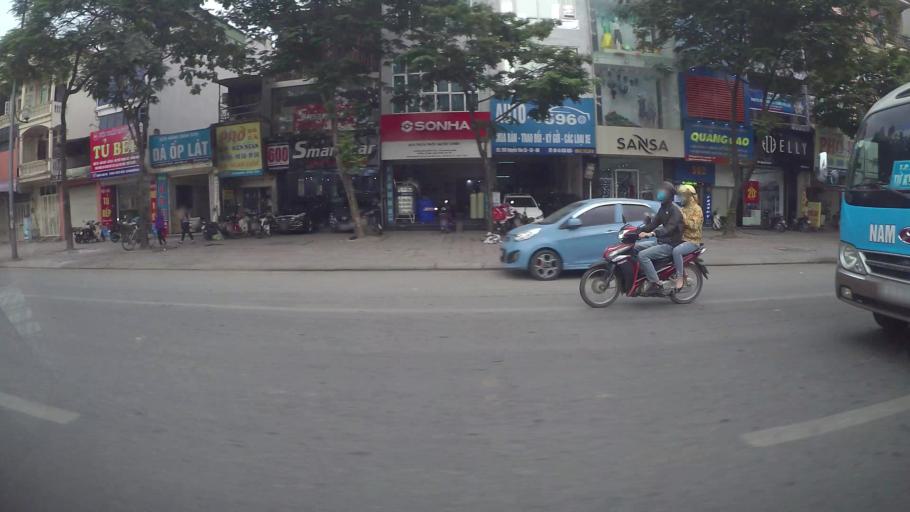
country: VN
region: Ha Noi
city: Hoan Kiem
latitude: 21.0514
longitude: 105.8853
